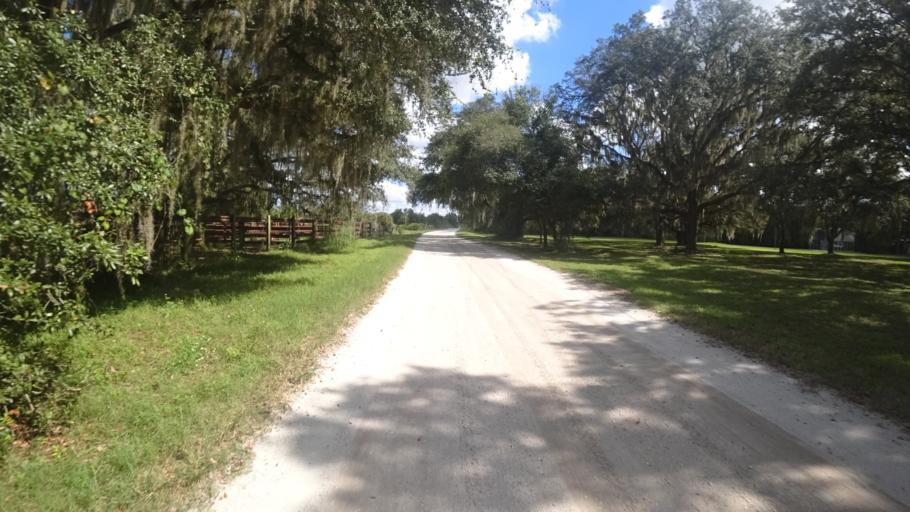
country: US
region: Florida
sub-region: Sarasota County
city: Lake Sarasota
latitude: 27.3205
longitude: -82.2608
